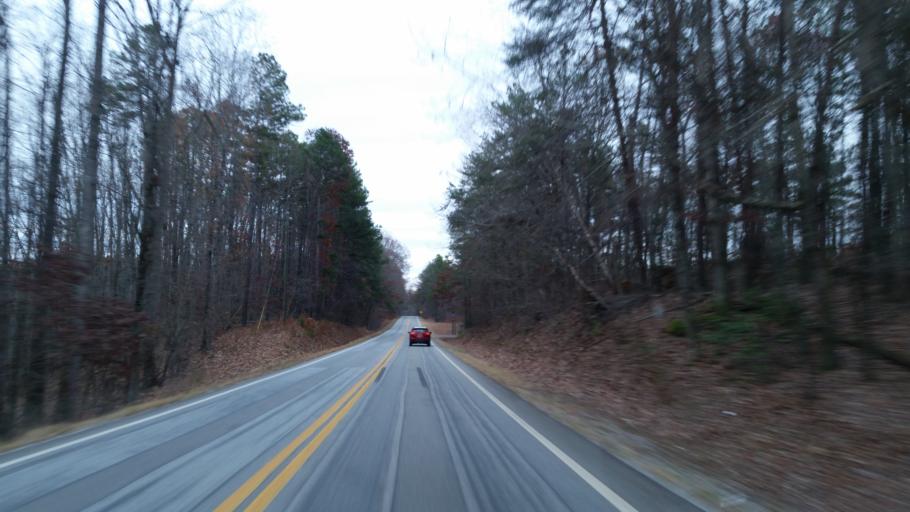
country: US
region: Georgia
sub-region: Dawson County
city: Dawsonville
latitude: 34.4221
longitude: -84.0400
